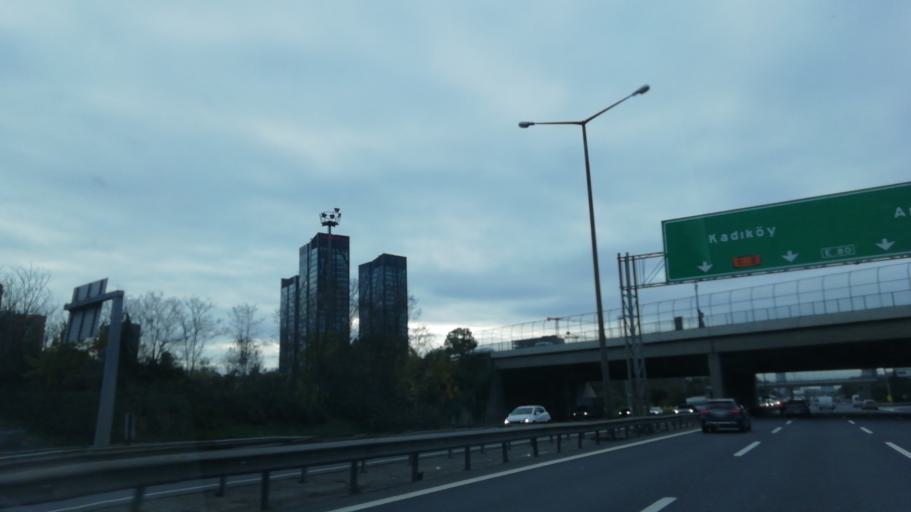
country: TR
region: Istanbul
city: Umraniye
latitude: 41.0308
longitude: 29.1209
